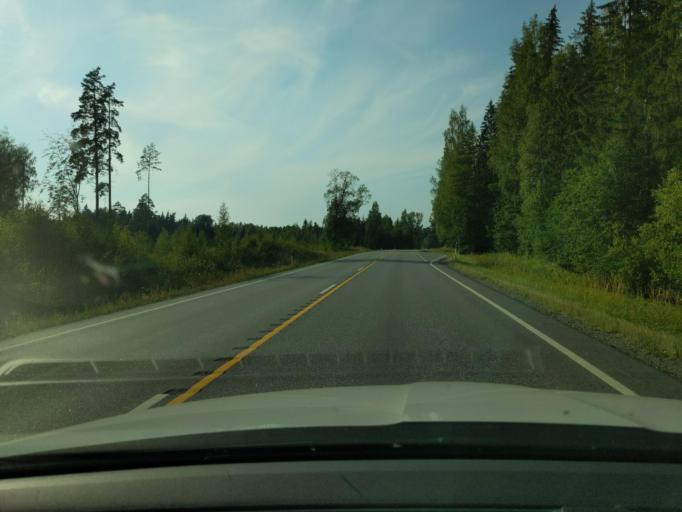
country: FI
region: Paijanne Tavastia
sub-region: Lahti
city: Padasjoki
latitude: 61.3198
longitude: 25.2832
